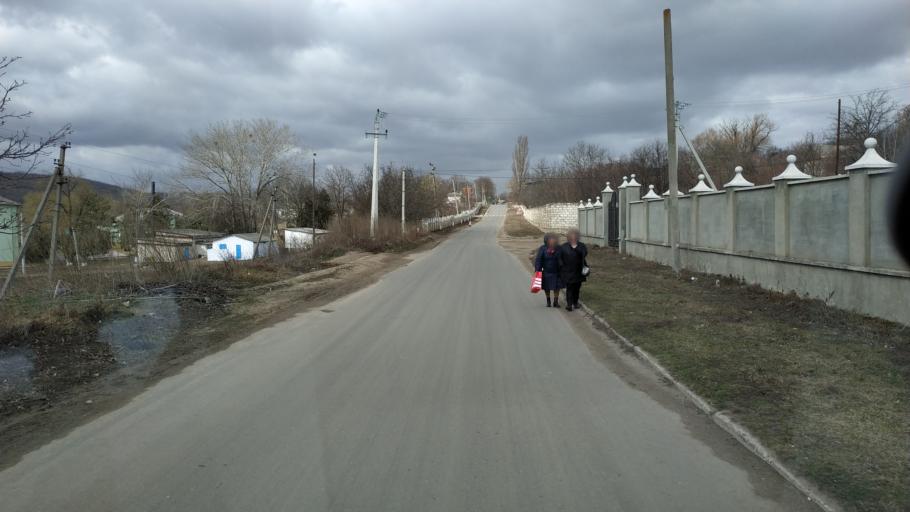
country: MD
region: Stinga Nistrului
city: Bucovat
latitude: 47.2256
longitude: 28.4366
